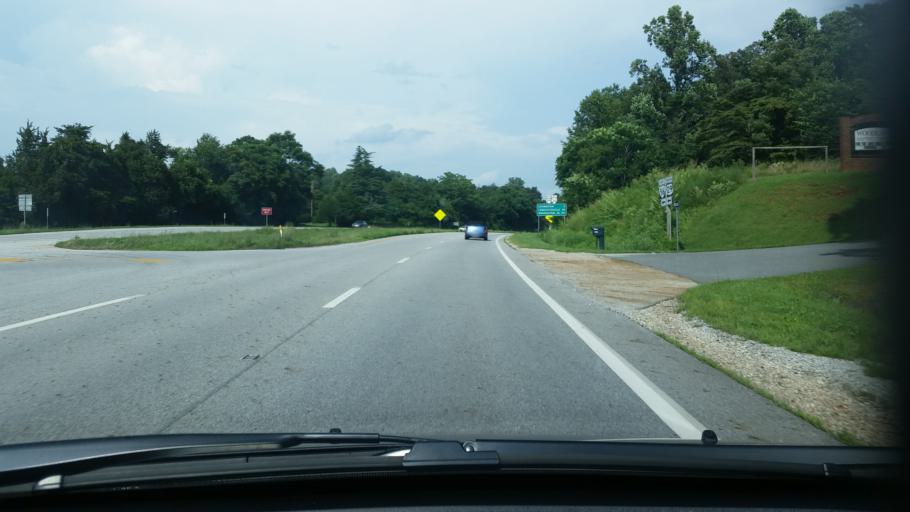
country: US
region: Virginia
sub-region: Nelson County
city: Lovingston
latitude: 37.7108
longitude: -78.9282
